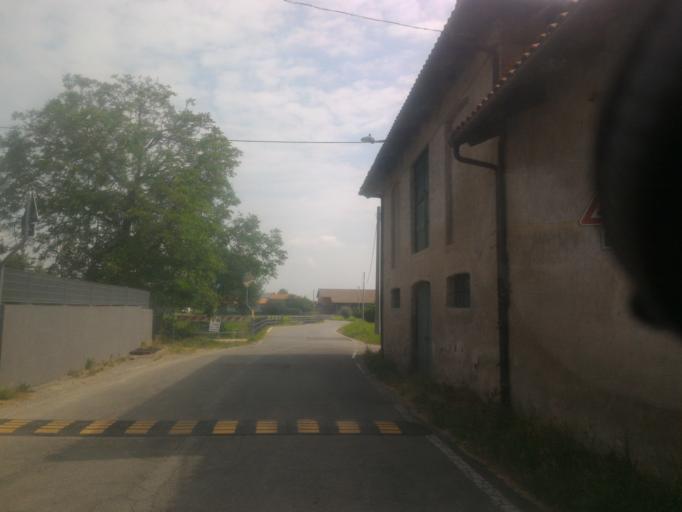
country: IT
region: Piedmont
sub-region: Provincia di Torino
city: San Secondo di Pinerolo
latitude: 44.8623
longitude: 7.3206
